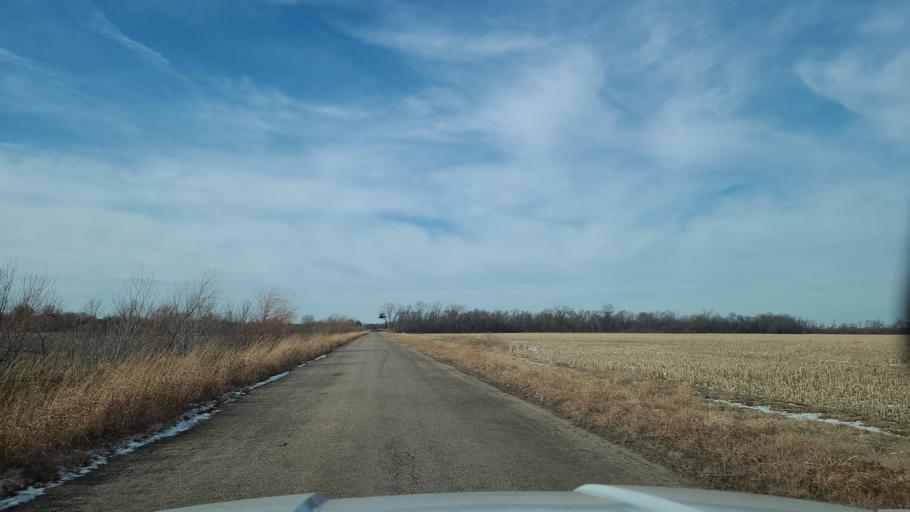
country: US
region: Kansas
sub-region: Douglas County
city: Lawrence
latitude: 38.9100
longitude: -95.2063
